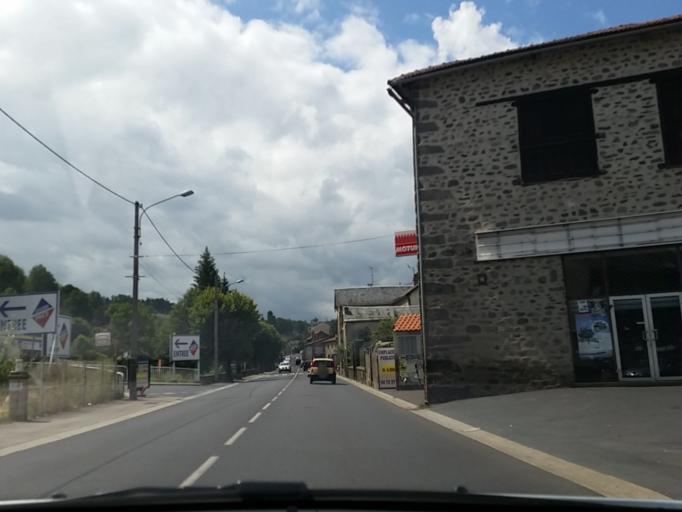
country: FR
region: Auvergne
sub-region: Departement du Cantal
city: Saint-Flour
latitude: 45.0321
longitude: 3.0994
